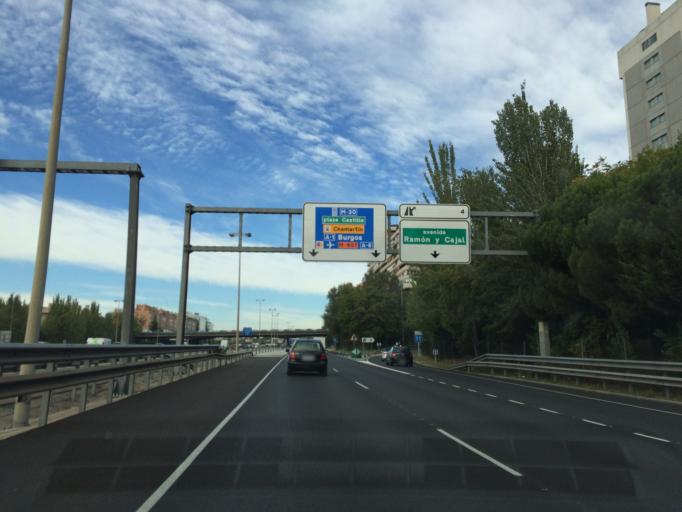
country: ES
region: Madrid
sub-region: Provincia de Madrid
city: Ciudad Lineal
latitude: 40.4505
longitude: -3.6623
